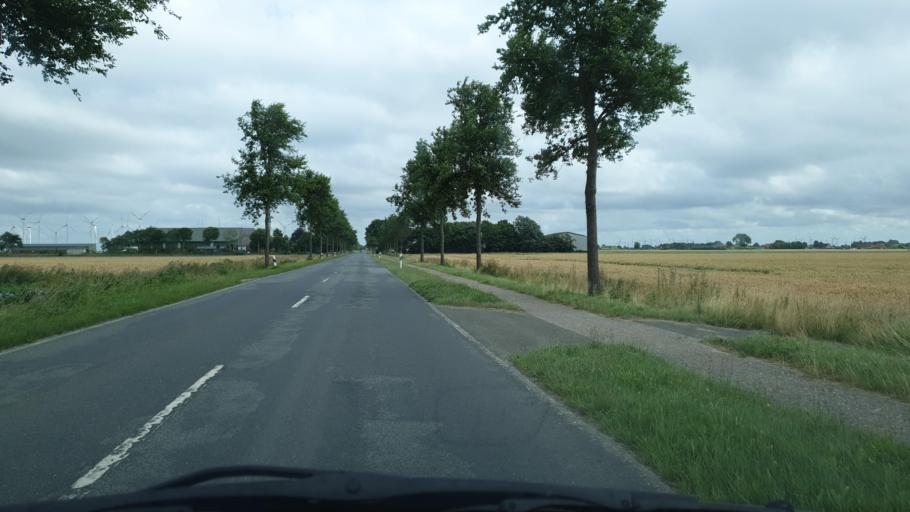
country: DE
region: Schleswig-Holstein
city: Friedrichskoog
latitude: 54.0198
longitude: 8.8824
